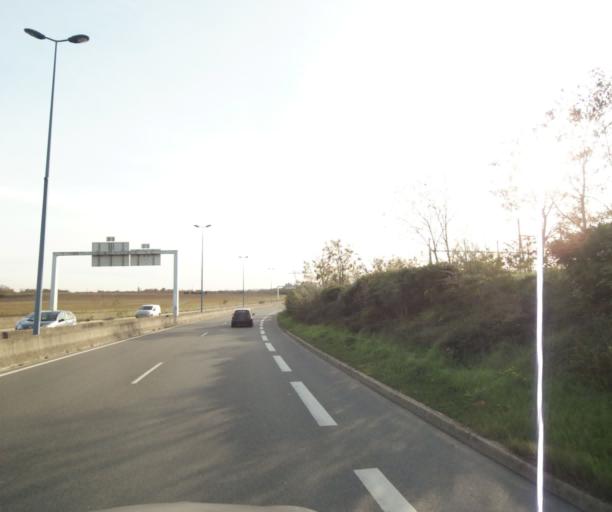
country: FR
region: Ile-de-France
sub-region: Departement des Yvelines
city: Triel-sur-Seine
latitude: 48.9675
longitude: 2.0140
